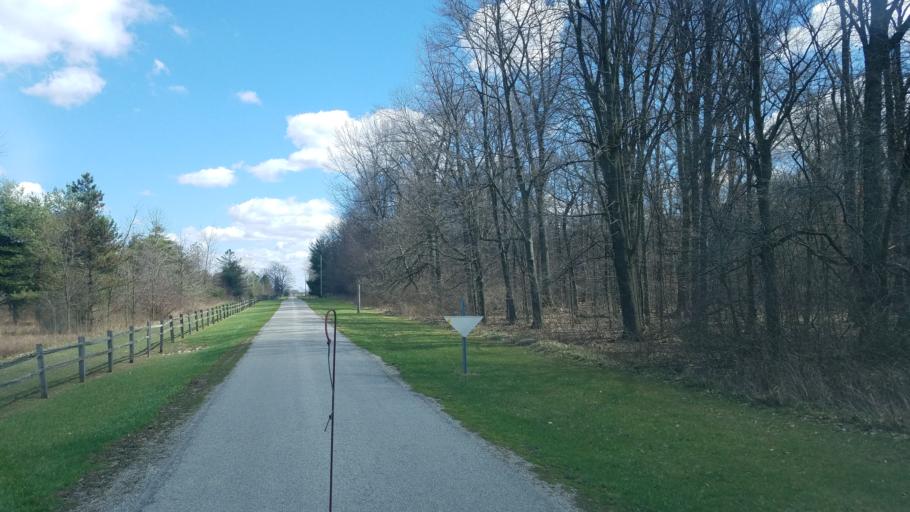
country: US
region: Ohio
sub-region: Hancock County
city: Arlington
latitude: 40.9545
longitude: -83.5408
